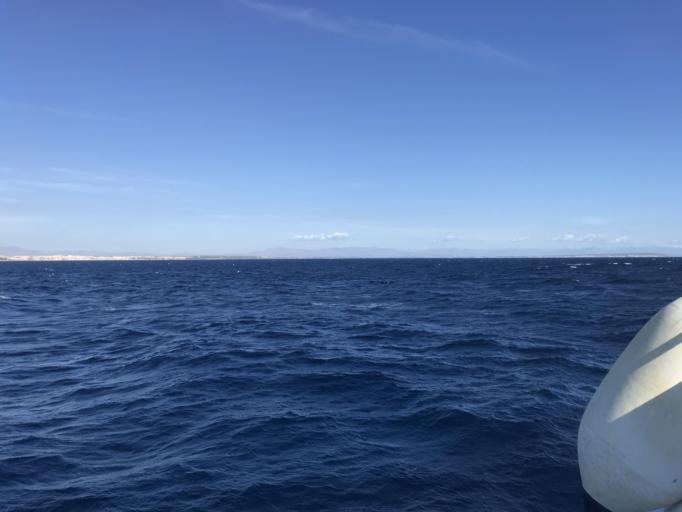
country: ES
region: Valencia
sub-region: Provincia de Alicante
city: Guardamar del Segura
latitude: 38.0330
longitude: -0.6130
